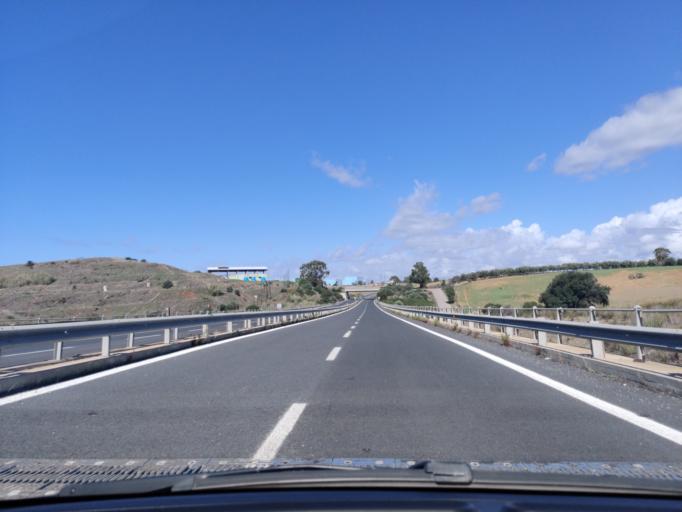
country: IT
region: Latium
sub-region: Citta metropolitana di Roma Capitale
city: Aurelia
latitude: 42.1171
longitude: 11.7918
